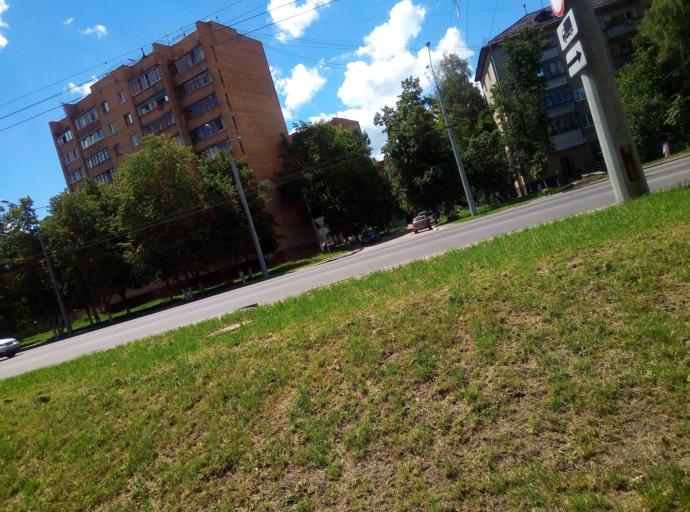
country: RU
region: Kursk
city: Kursk
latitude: 51.7676
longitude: 36.1830
